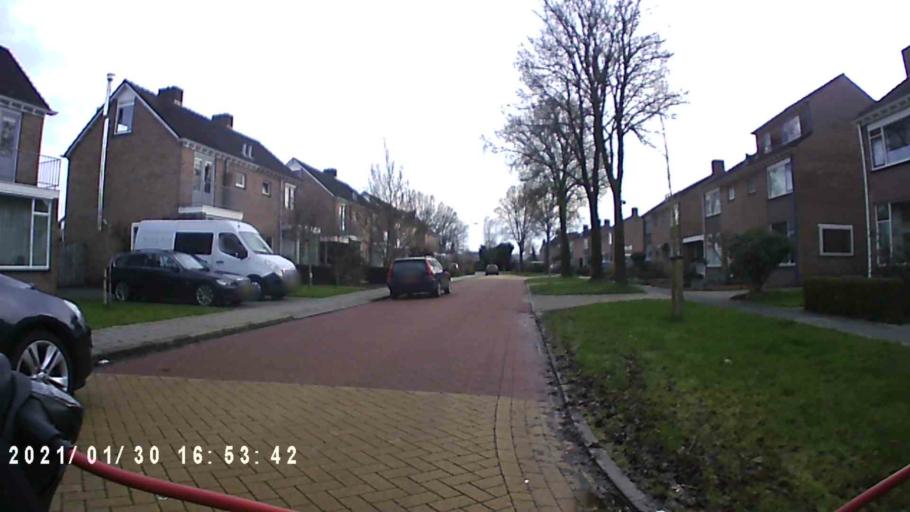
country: NL
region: Groningen
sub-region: Gemeente Leek
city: Leek
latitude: 53.1581
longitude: 6.3804
